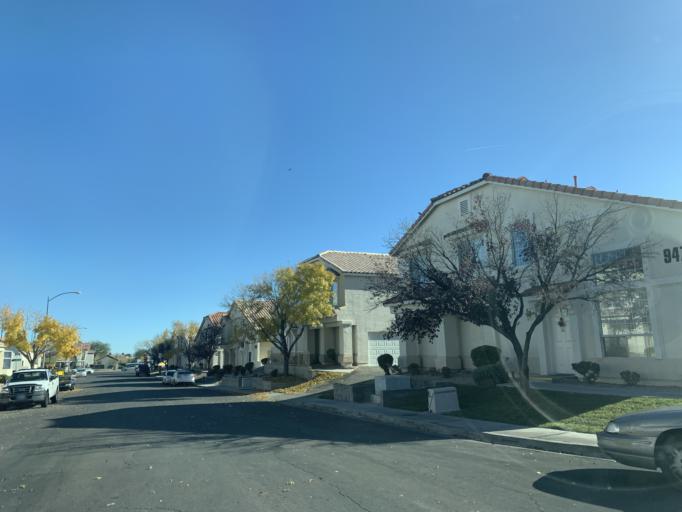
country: US
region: Nevada
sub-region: Clark County
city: Summerlin South
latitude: 36.1211
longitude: -115.2987
